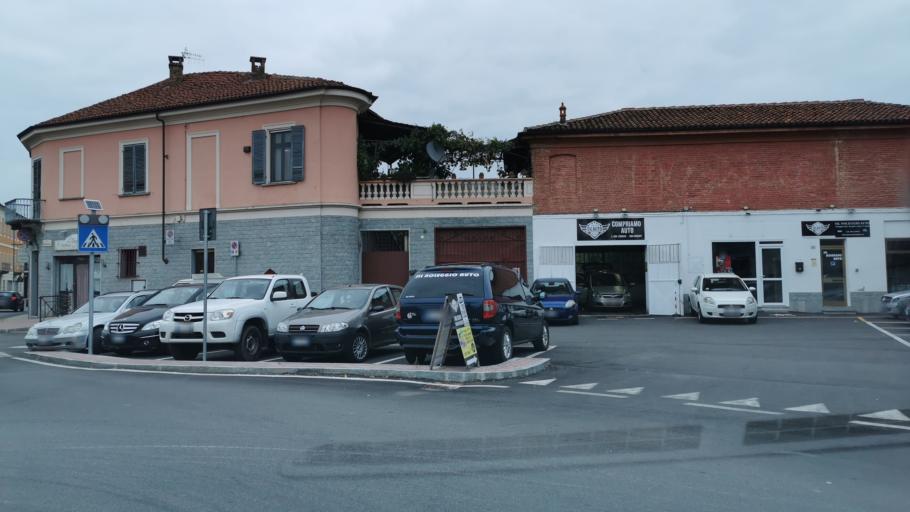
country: IT
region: Piedmont
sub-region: Provincia di Cuneo
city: Bra
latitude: 44.6903
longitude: 7.8549
